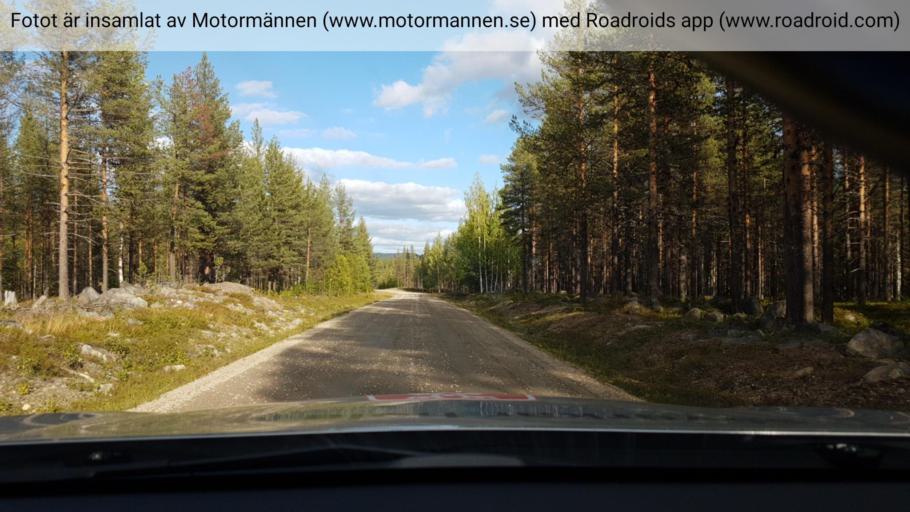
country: SE
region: Vaesterbotten
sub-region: Sorsele Kommun
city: Sorsele
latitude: 65.3621
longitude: 18.0403
